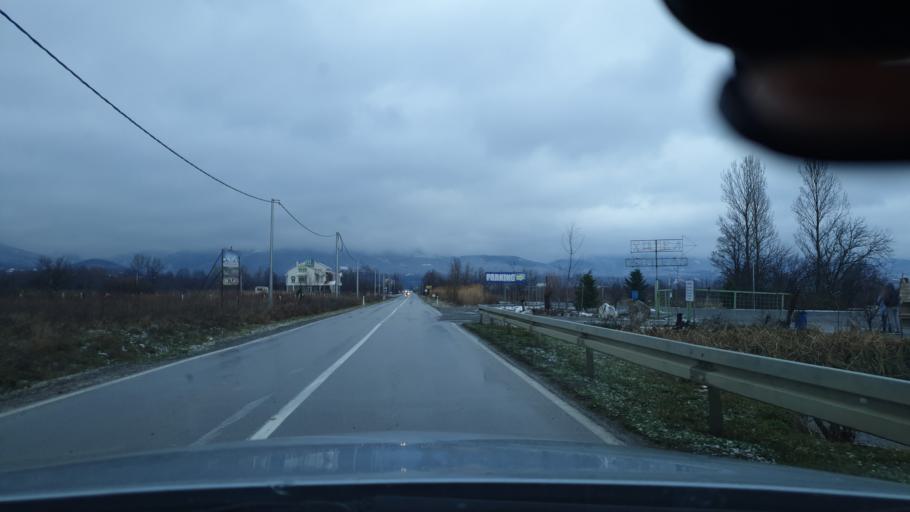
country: RS
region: Central Serbia
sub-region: Branicevski Okrug
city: Petrovac
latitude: 44.3068
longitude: 21.4845
